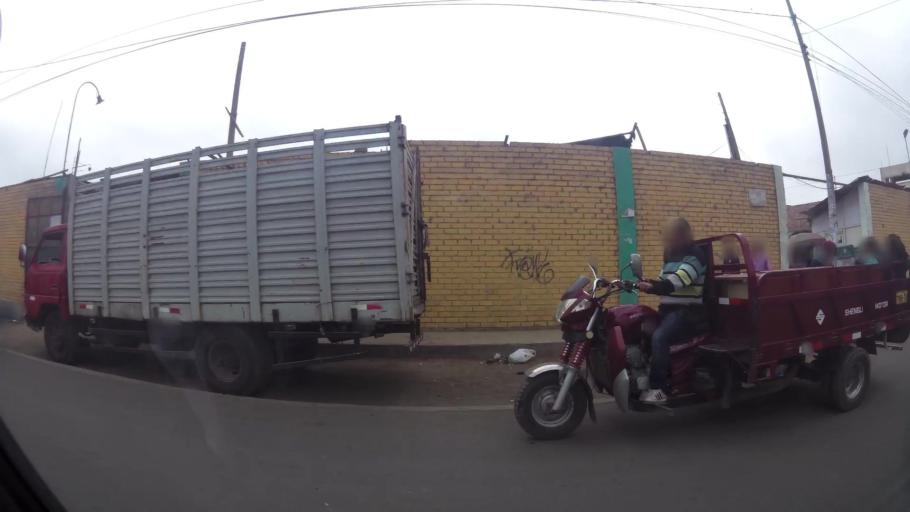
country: PE
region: Lima
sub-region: Provincia de Huaral
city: Huaral
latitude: -11.5006
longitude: -77.2050
